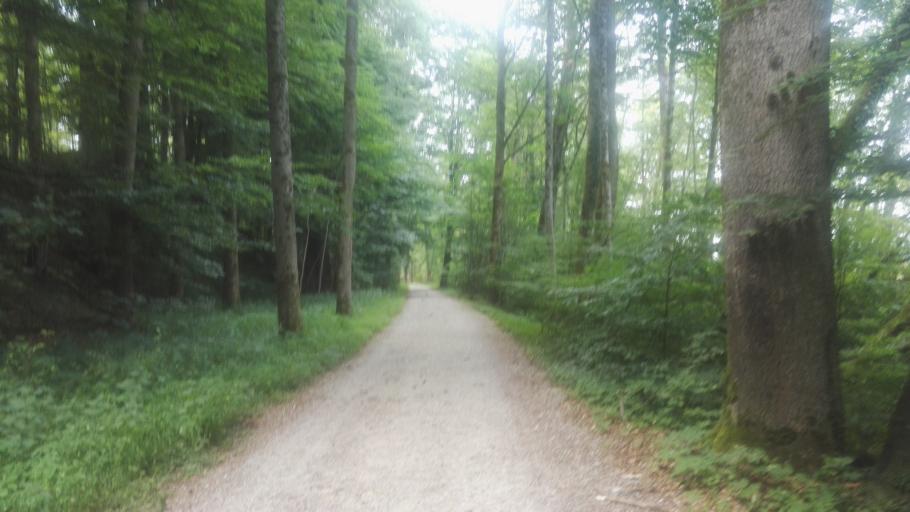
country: DE
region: Bavaria
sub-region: Upper Bavaria
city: Chiemsee
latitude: 47.8614
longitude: 12.4083
